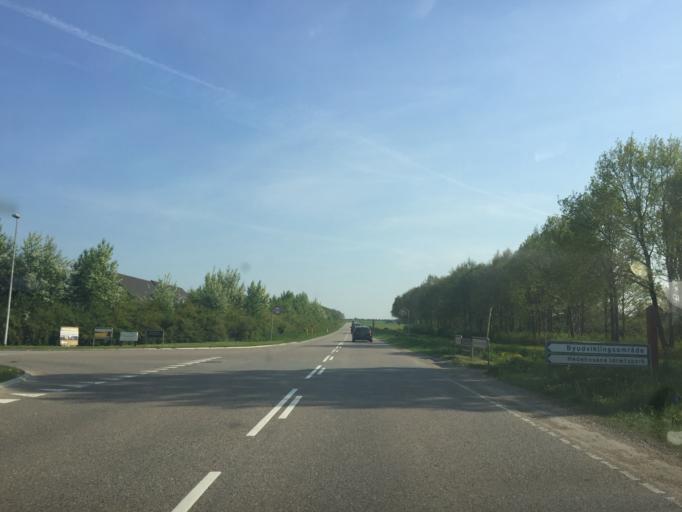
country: DK
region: Capital Region
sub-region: Hoje-Taastrup Kommune
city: Flong
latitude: 55.6412
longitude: 12.1918
